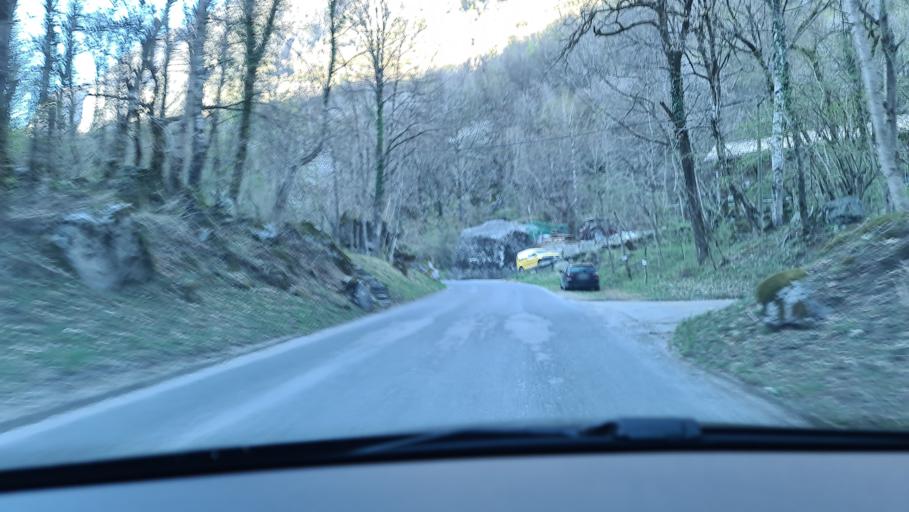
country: CH
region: Ticino
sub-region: Vallemaggia District
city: Cevio
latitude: 46.3615
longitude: 8.5768
